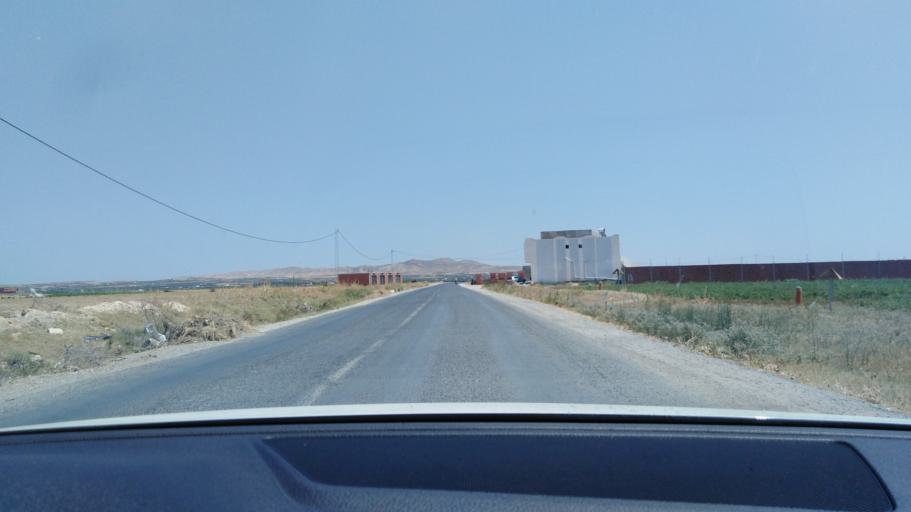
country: TN
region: Al Qayrawan
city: Sbikha
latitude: 36.1136
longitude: 10.1002
